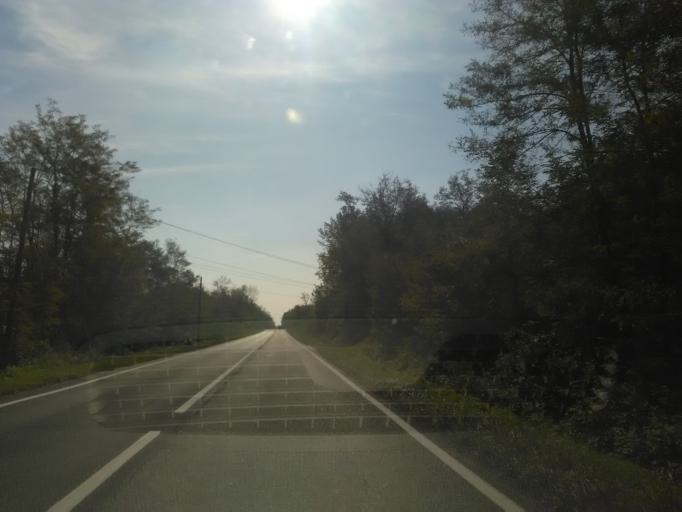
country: IT
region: Piedmont
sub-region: Provincia di Vercelli
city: Gattinara
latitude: 45.5882
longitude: 8.3726
